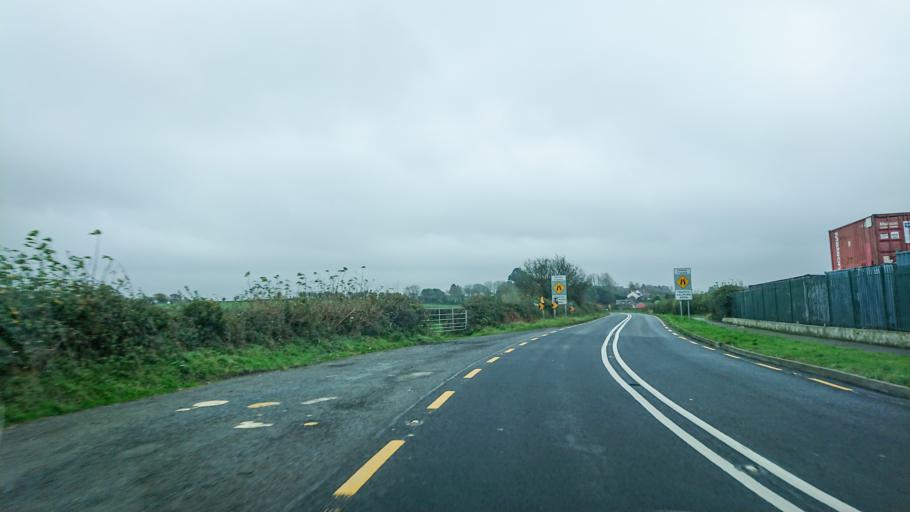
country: IE
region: Leinster
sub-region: Kilkenny
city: Mooncoin
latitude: 52.3009
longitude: -7.2699
